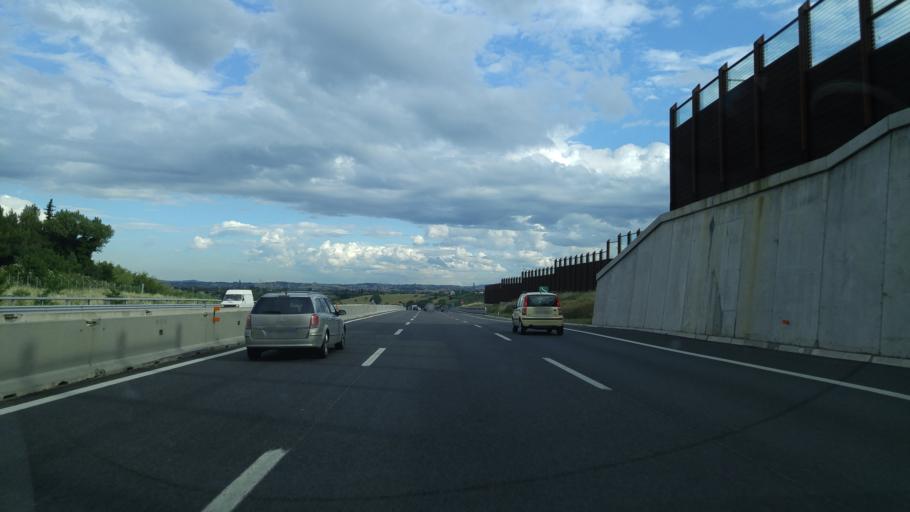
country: IT
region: Emilia-Romagna
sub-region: Provincia di Rimini
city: Rivazzurra
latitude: 44.0193
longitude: 12.5852
